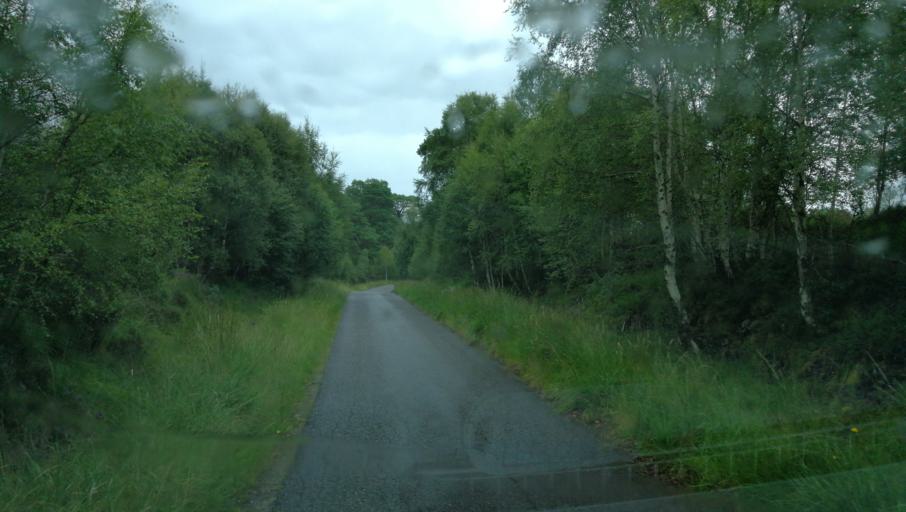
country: GB
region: Scotland
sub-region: Highland
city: Spean Bridge
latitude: 57.2670
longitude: -4.9751
